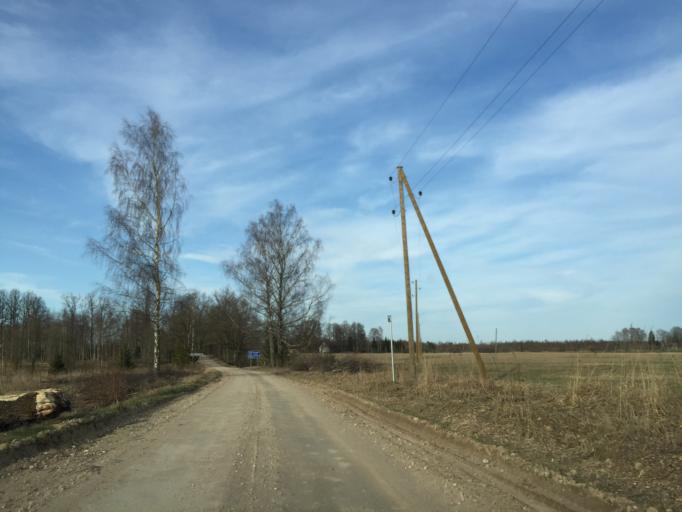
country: LV
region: Kegums
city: Kegums
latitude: 56.8046
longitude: 24.7765
